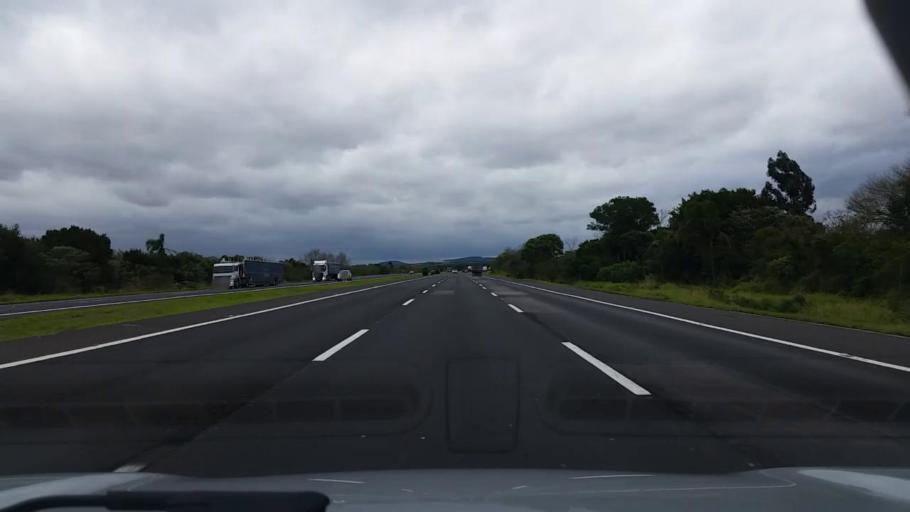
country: BR
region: Rio Grande do Sul
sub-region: Osorio
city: Osorio
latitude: -29.8782
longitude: -50.4297
